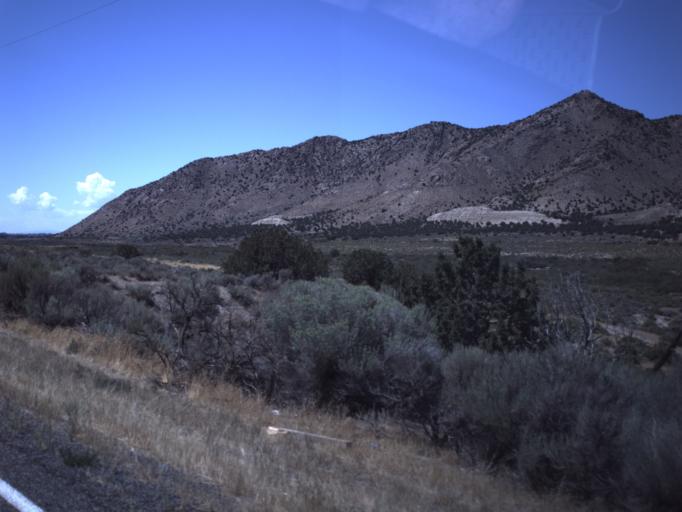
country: US
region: Utah
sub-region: Millard County
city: Delta
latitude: 39.5503
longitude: -112.2243
